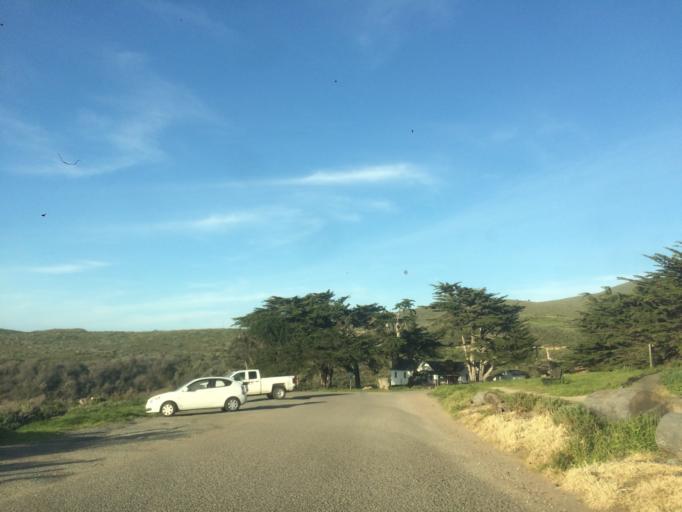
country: US
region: California
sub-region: San Luis Obispo County
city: Los Osos
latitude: 35.2733
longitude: -120.8881
